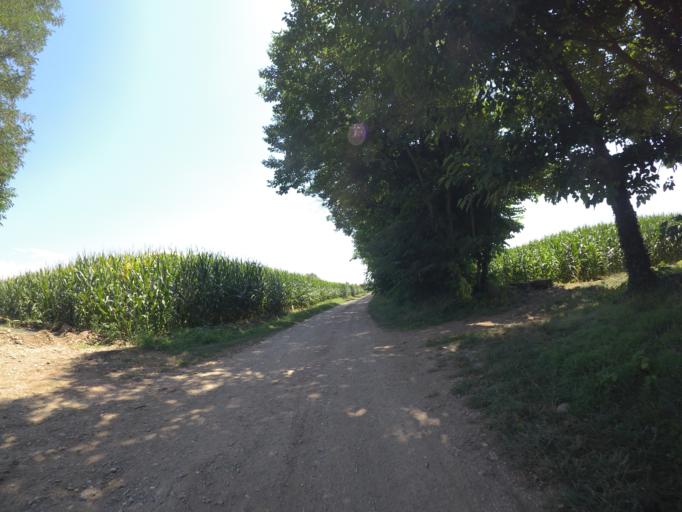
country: IT
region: Friuli Venezia Giulia
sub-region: Provincia di Udine
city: Mortegliano
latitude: 45.9349
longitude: 13.1836
